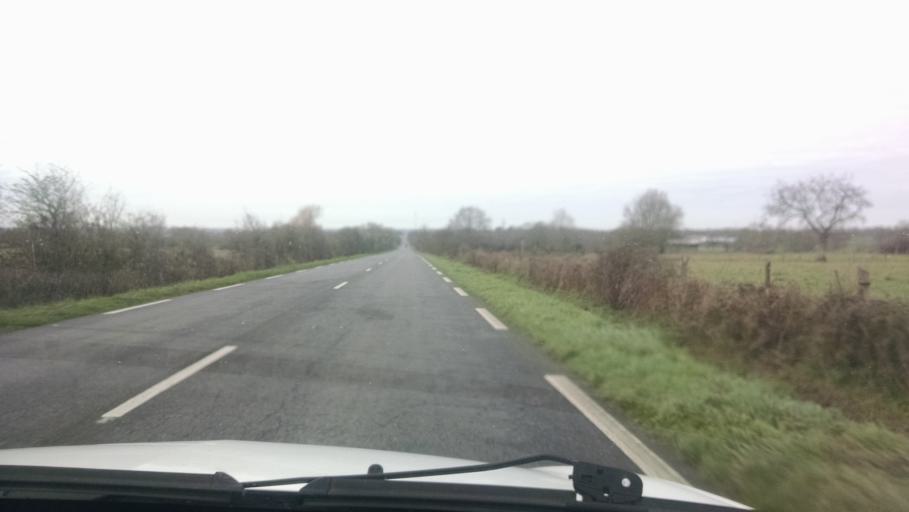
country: FR
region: Pays de la Loire
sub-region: Departement de la Loire-Atlantique
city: Getigne
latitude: 47.0698
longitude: -1.2138
